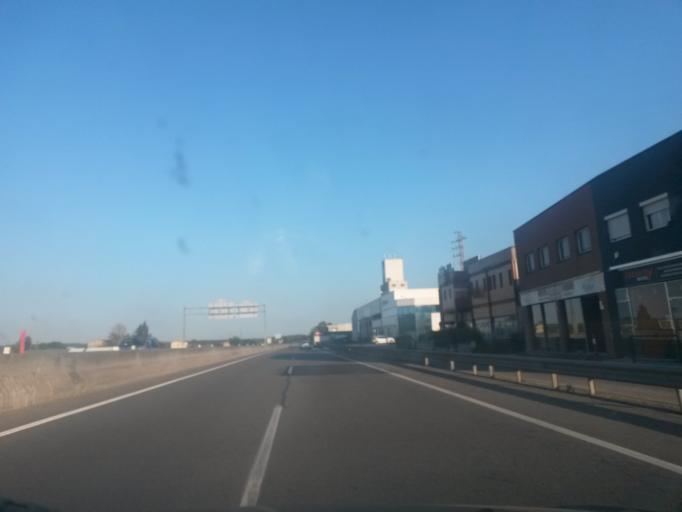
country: ES
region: Catalonia
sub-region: Provincia de Girona
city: Cornella del Terri
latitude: 42.0941
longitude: 2.8024
